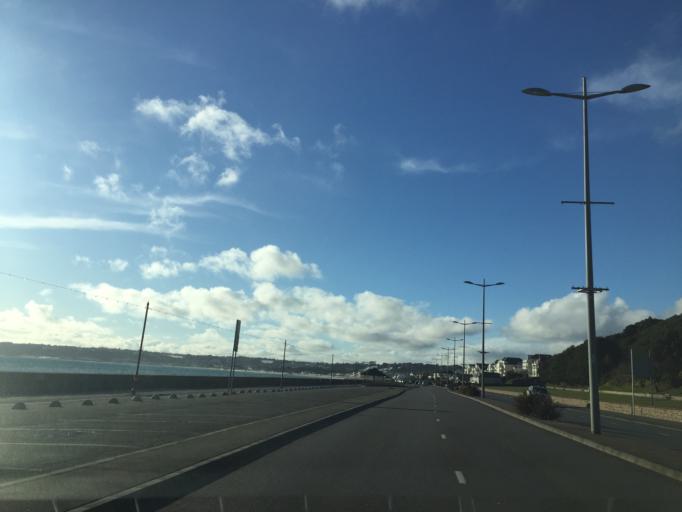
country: JE
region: St Helier
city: Saint Helier
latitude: 49.1886
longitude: -2.1186
